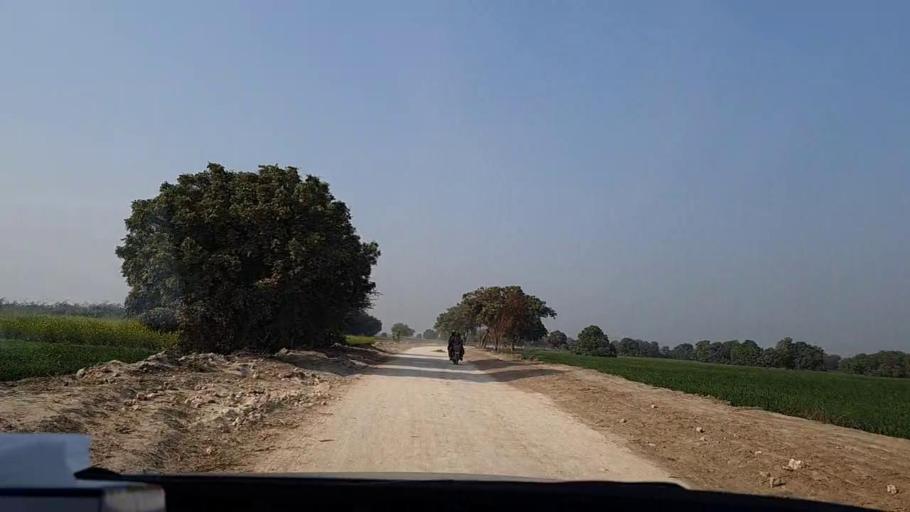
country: PK
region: Sindh
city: Tando Ghulam Ali
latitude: 25.1437
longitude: 68.8770
